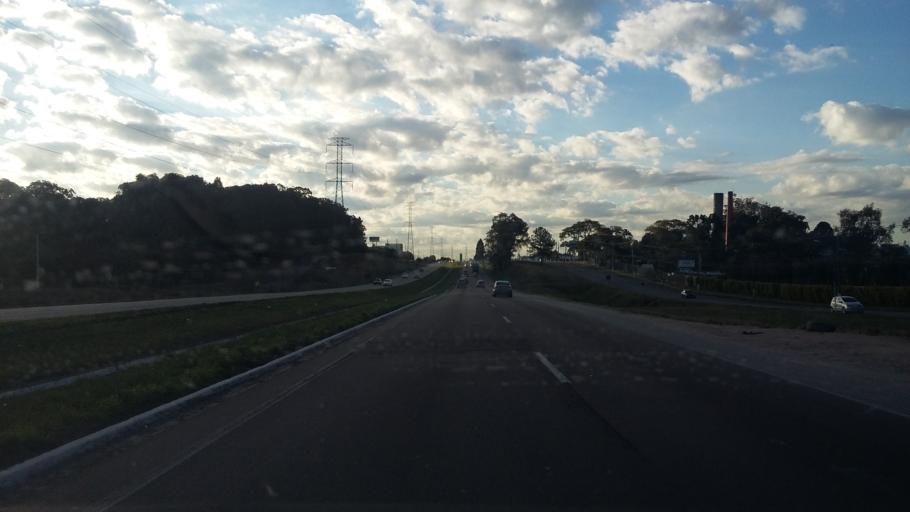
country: BR
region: Parana
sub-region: Curitiba
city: Curitiba
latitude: -25.4632
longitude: -49.3577
